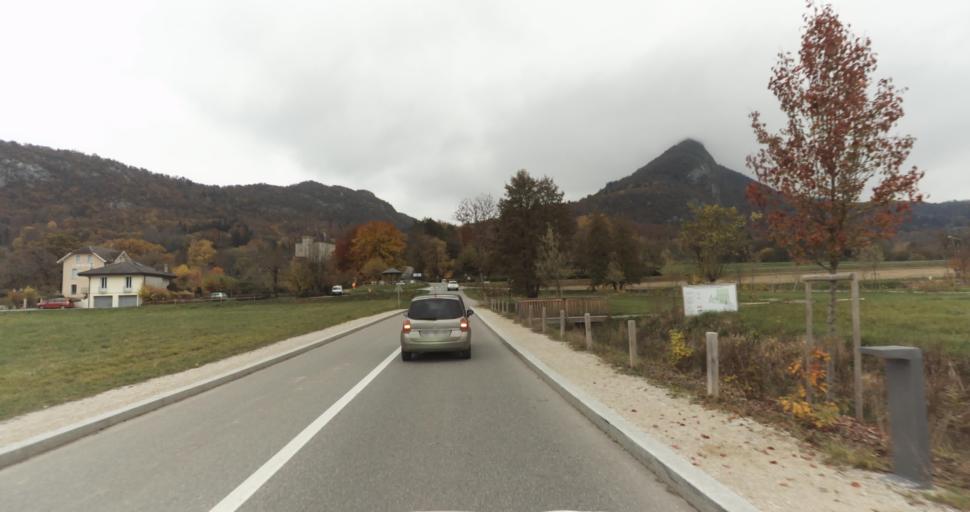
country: FR
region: Rhone-Alpes
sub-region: Departement de la Haute-Savoie
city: Talloires
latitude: 45.8269
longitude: 6.1963
